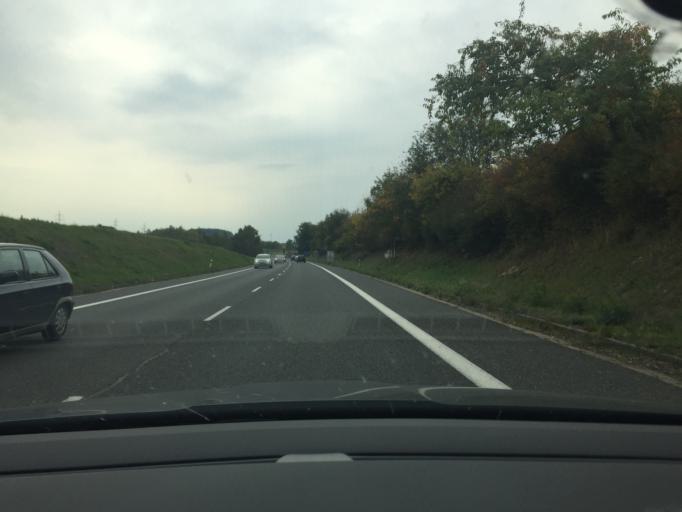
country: CZ
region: Central Bohemia
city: Milin
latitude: 49.6433
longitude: 14.0503
